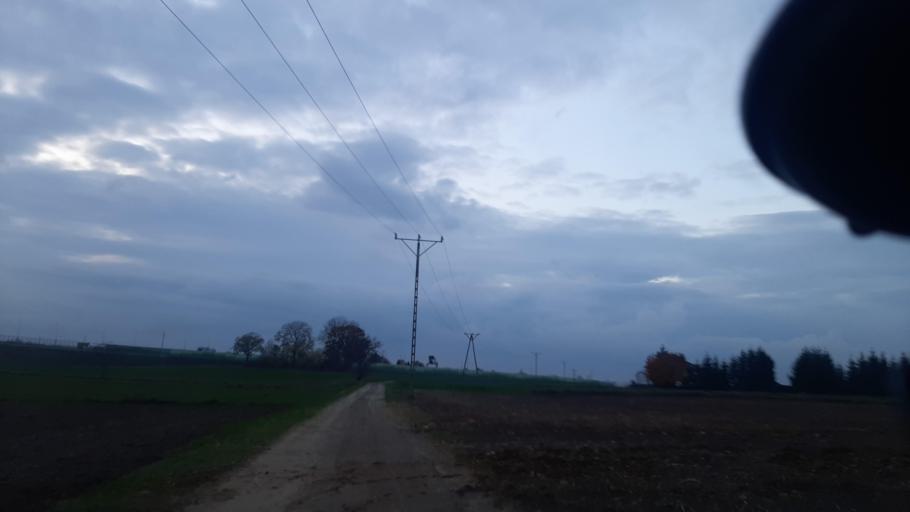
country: PL
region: Lublin Voivodeship
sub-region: Powiat lubelski
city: Jastkow
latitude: 51.3308
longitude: 22.3936
